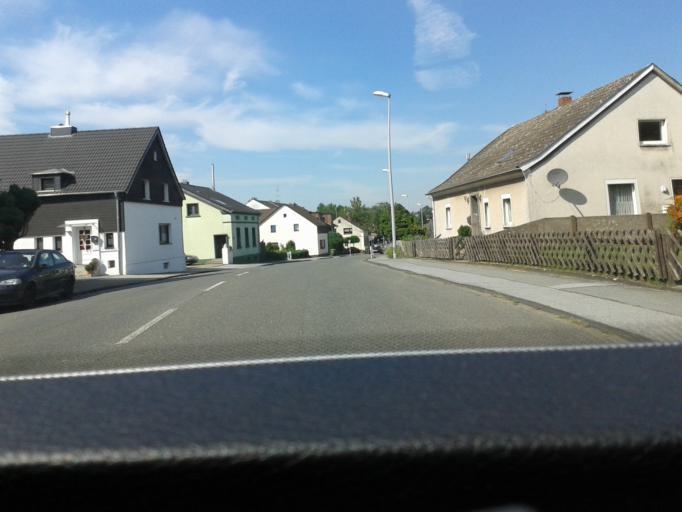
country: DE
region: North Rhine-Westphalia
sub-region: Regierungsbezirk Dusseldorf
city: Muelheim (Ruhr)
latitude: 51.4123
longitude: 6.8603
